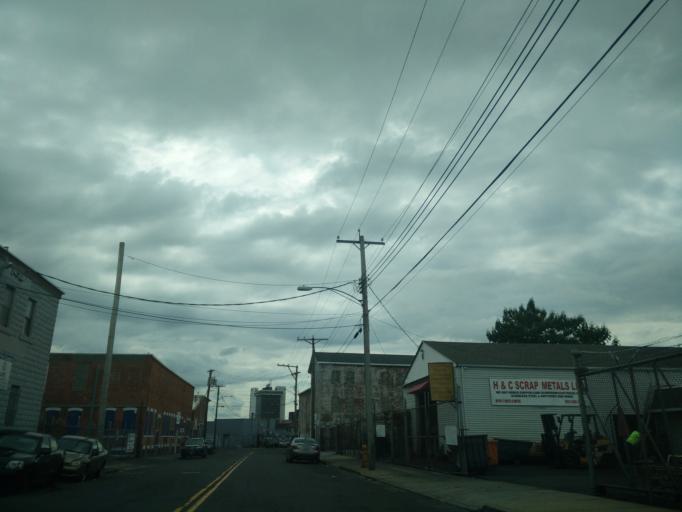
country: US
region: Connecticut
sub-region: Fairfield County
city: Bridgeport
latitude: 41.1856
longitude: -73.1876
